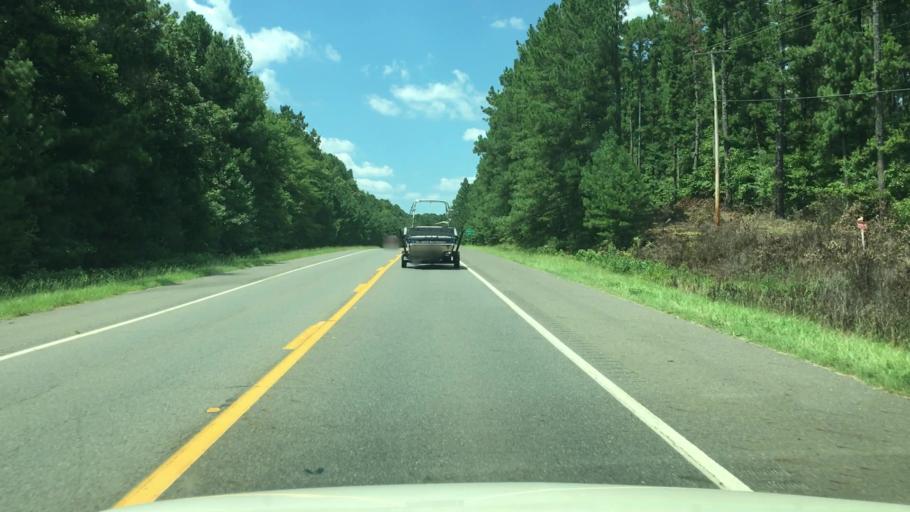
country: US
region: Arkansas
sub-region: Clark County
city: Arkadelphia
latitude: 34.1956
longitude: -93.0753
